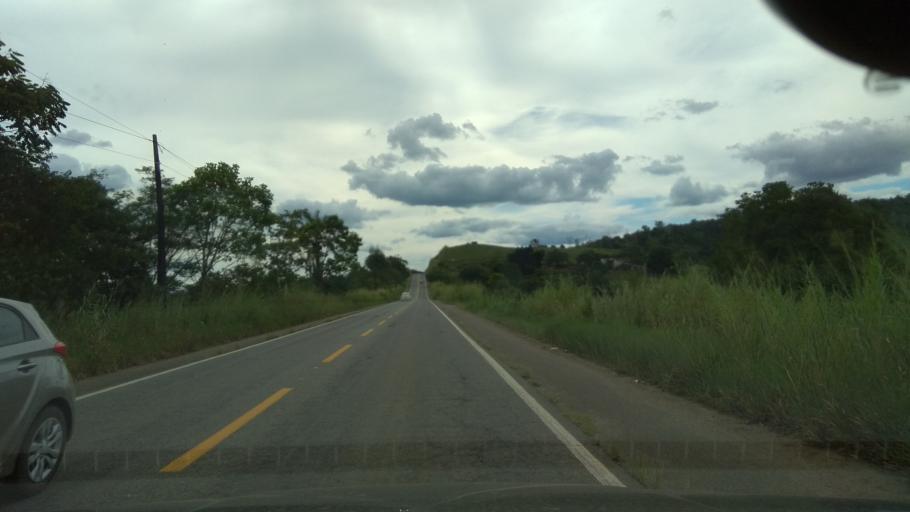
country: BR
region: Bahia
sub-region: Ipiau
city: Ipiau
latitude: -14.1587
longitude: -39.6937
